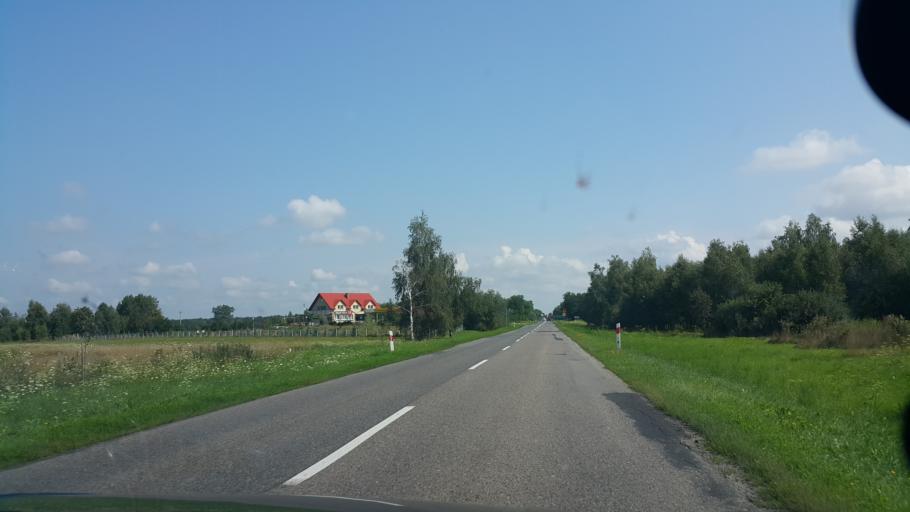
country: PL
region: Lublin Voivodeship
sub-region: Powiat wlodawski
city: Urszulin
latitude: 51.3819
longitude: 23.1879
